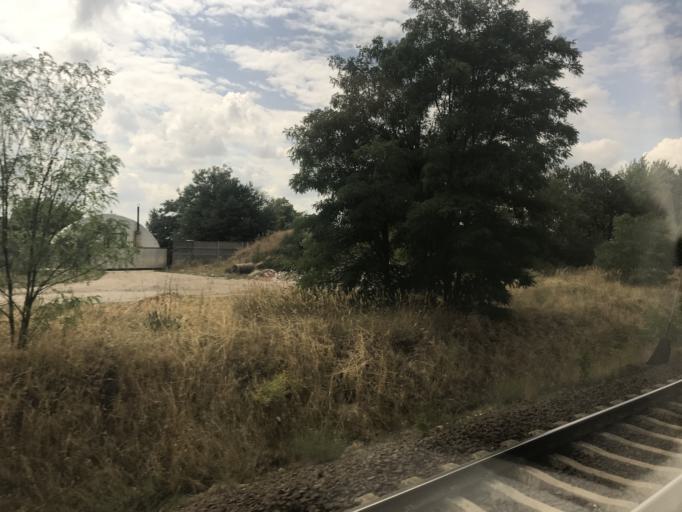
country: PL
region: Greater Poland Voivodeship
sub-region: Powiat poznanski
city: Buk
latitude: 52.3468
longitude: 16.5934
